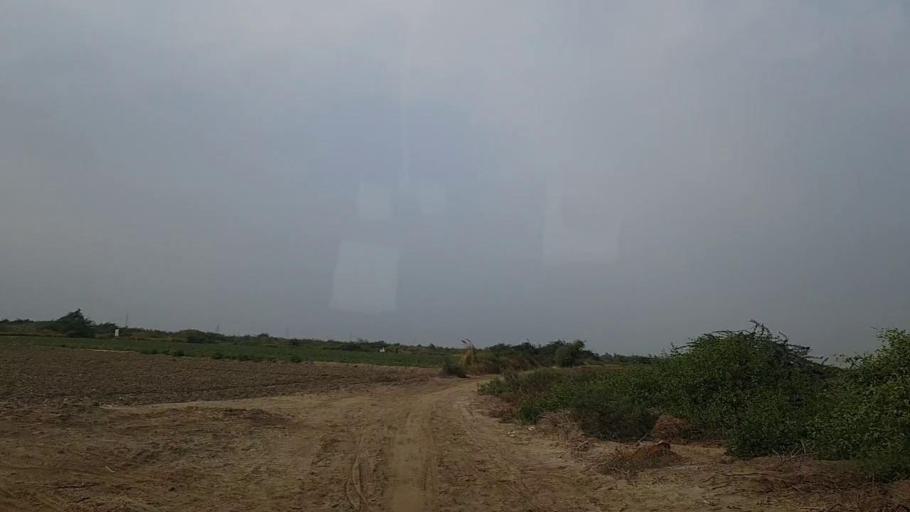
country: PK
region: Sindh
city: Mirpur Sakro
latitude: 24.6185
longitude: 67.5040
